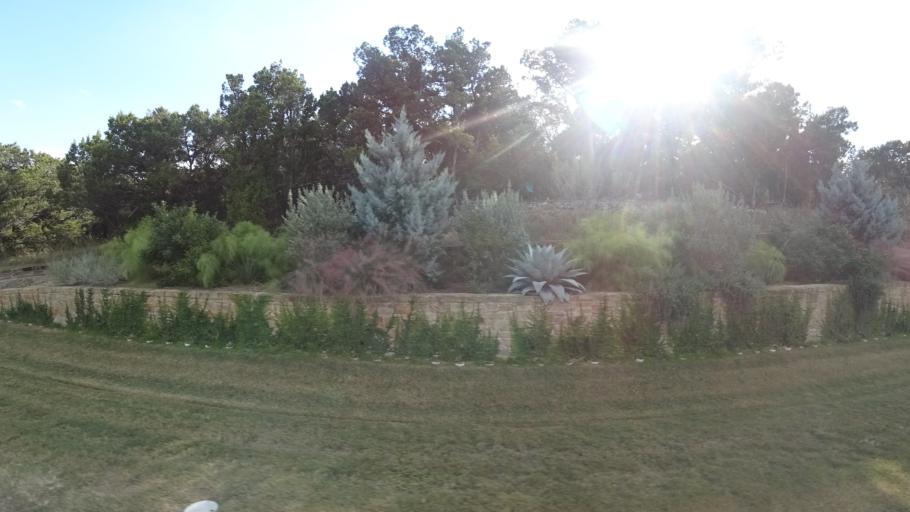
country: US
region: Texas
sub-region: Travis County
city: Barton Creek
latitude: 30.2738
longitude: -97.8811
